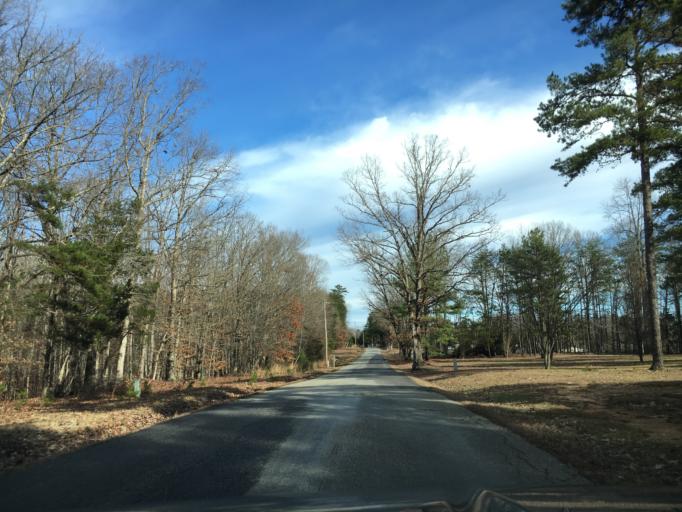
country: US
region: Virginia
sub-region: Nottoway County
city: Crewe
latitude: 37.2605
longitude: -78.2236
